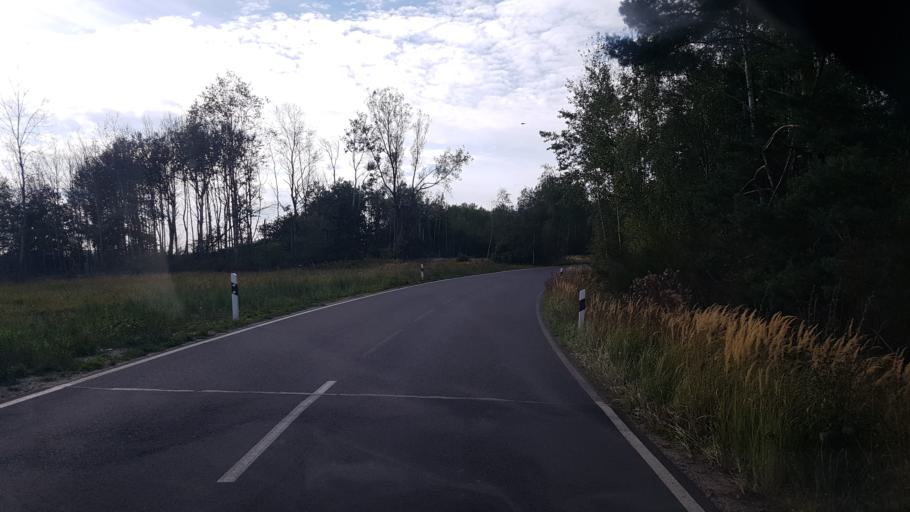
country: DE
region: Brandenburg
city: Welzow
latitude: 51.5341
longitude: 14.2456
